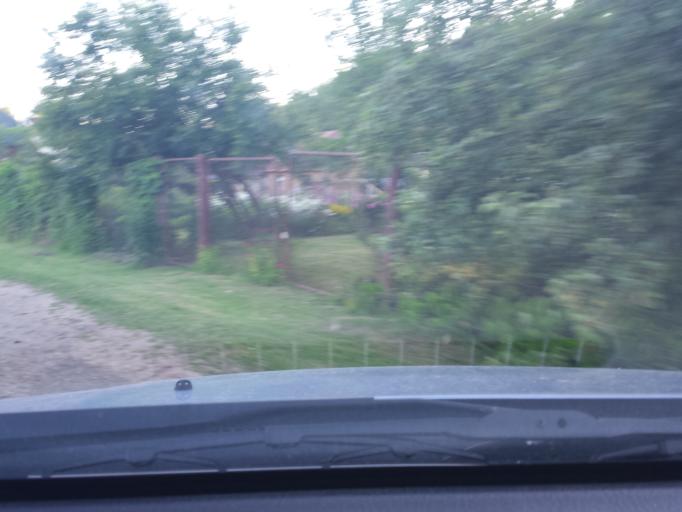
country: LV
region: Carnikava
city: Carnikava
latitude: 57.1269
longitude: 24.2395
